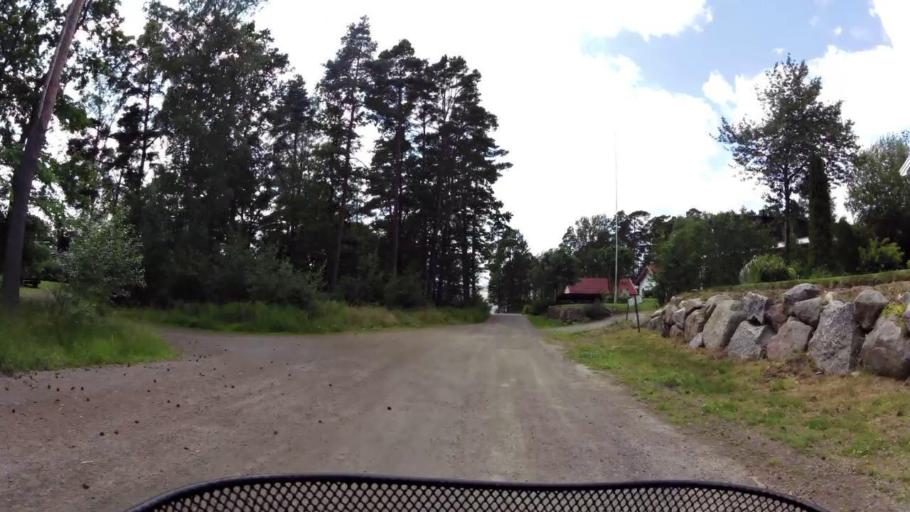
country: SE
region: OEstergoetland
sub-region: Linkopings Kommun
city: Ekangen
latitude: 58.4790
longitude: 15.6307
